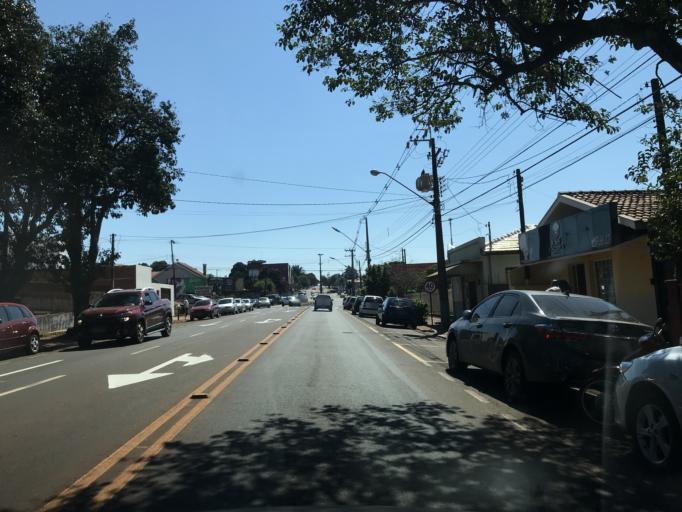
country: BR
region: Parana
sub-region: Toledo
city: Toledo
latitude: -24.7297
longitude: -53.7361
